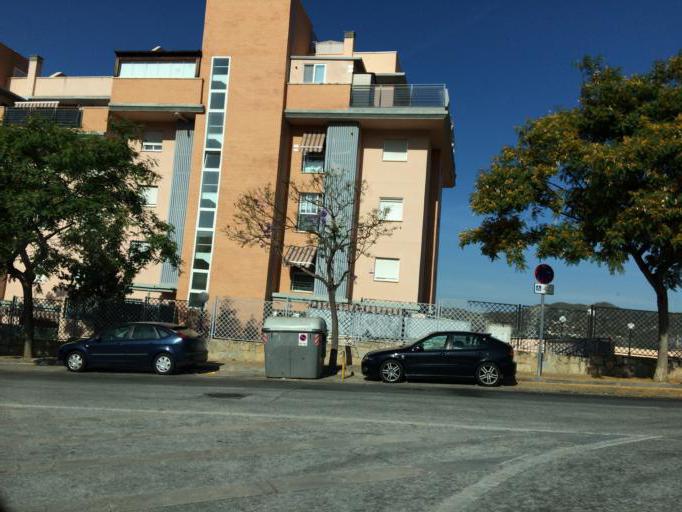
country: ES
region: Andalusia
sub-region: Provincia de Malaga
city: Malaga
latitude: 36.7532
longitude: -4.4191
